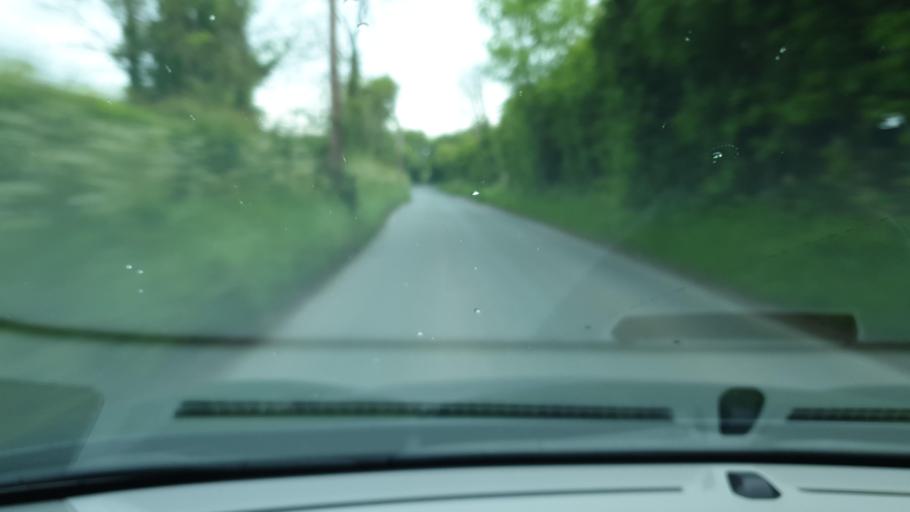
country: IE
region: Leinster
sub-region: An Mhi
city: Ashbourne
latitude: 53.5516
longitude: -6.3999
